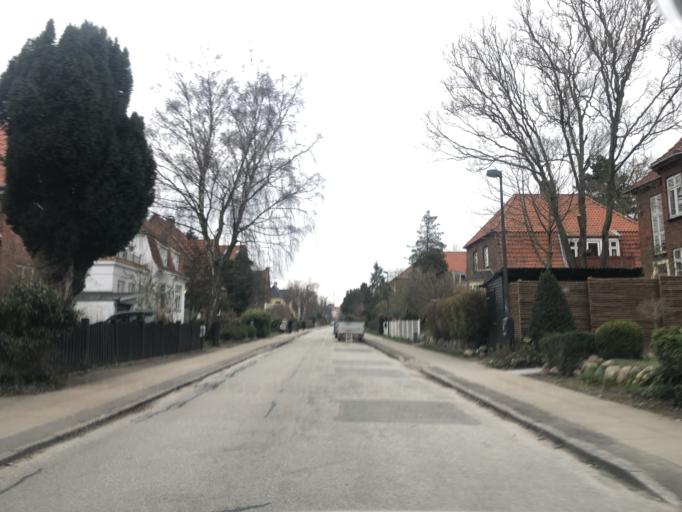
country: DK
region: Capital Region
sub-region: Frederiksberg Kommune
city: Frederiksberg
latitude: 55.6537
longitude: 12.5229
